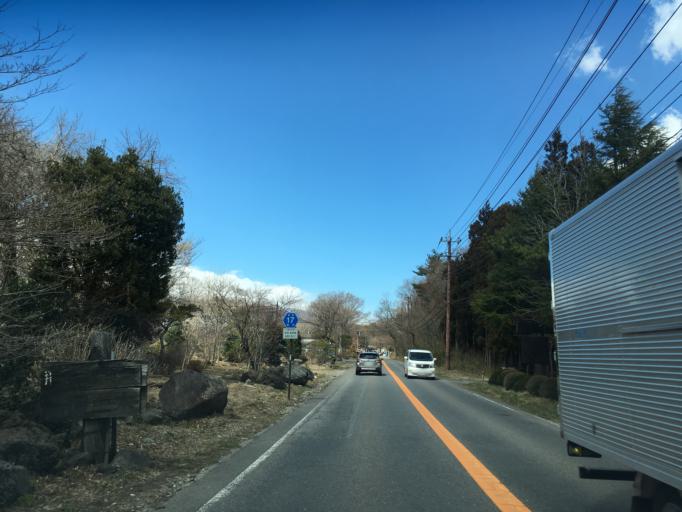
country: JP
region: Tochigi
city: Kuroiso
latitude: 37.0499
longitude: 140.0141
